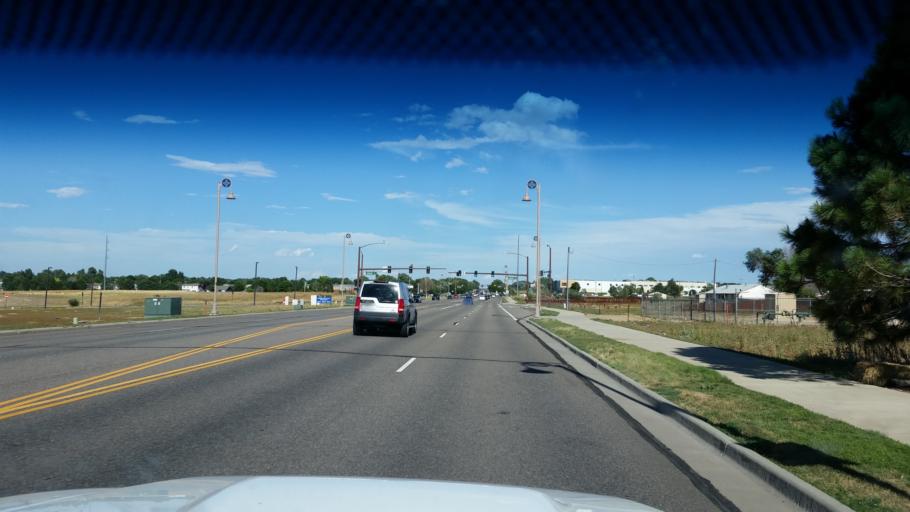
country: US
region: Colorado
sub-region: Adams County
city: Northglenn
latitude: 39.9285
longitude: -104.9833
